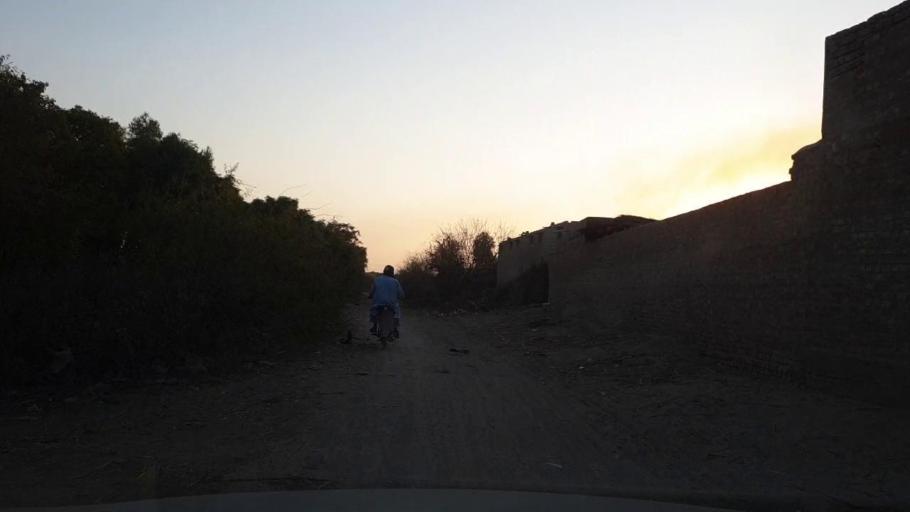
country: PK
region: Sindh
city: Tando Allahyar
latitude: 25.5465
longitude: 68.6356
